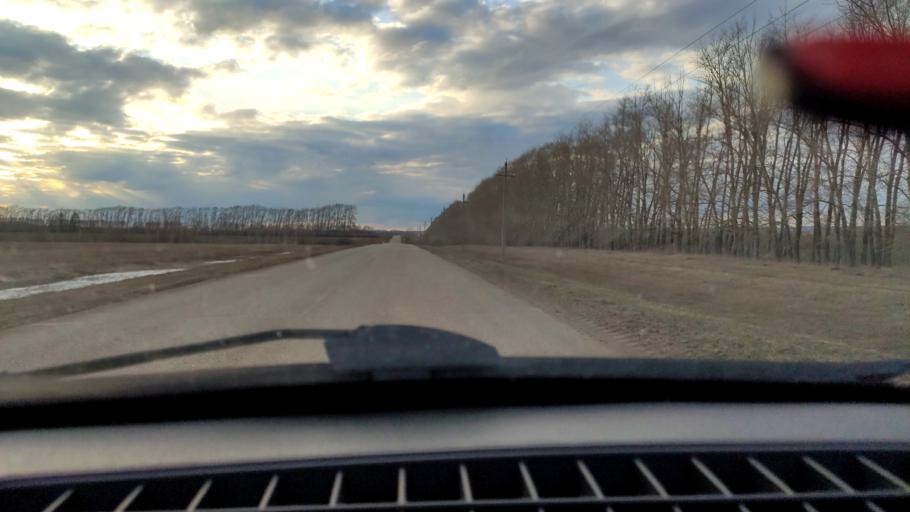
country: RU
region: Bashkortostan
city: Tolbazy
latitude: 53.9915
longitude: 55.7853
